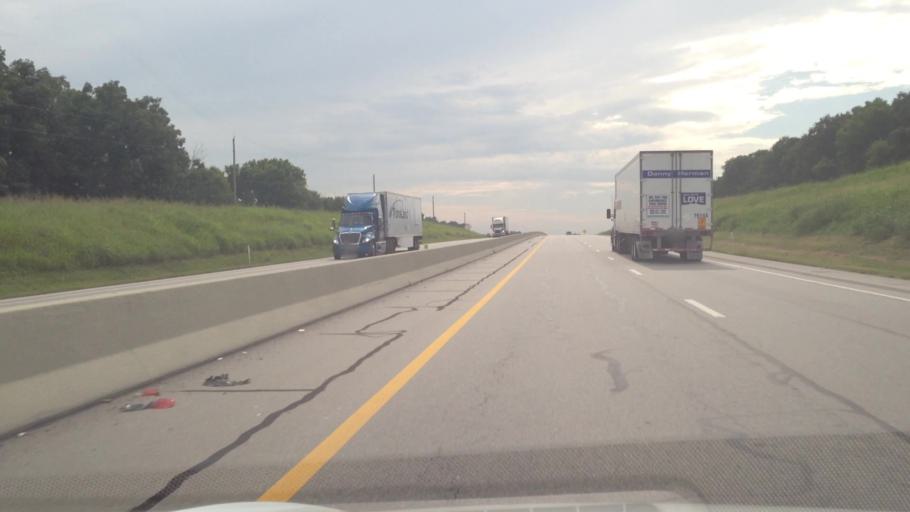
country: US
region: Kansas
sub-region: Cherokee County
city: Baxter Springs
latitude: 36.9252
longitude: -94.7442
